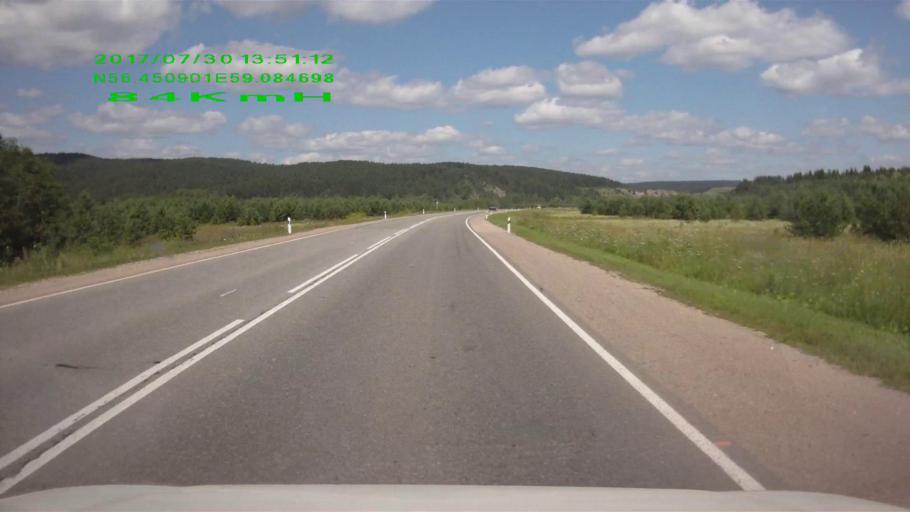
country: RU
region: Sverdlovsk
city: Mikhaylovsk
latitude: 56.4513
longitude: 59.0850
